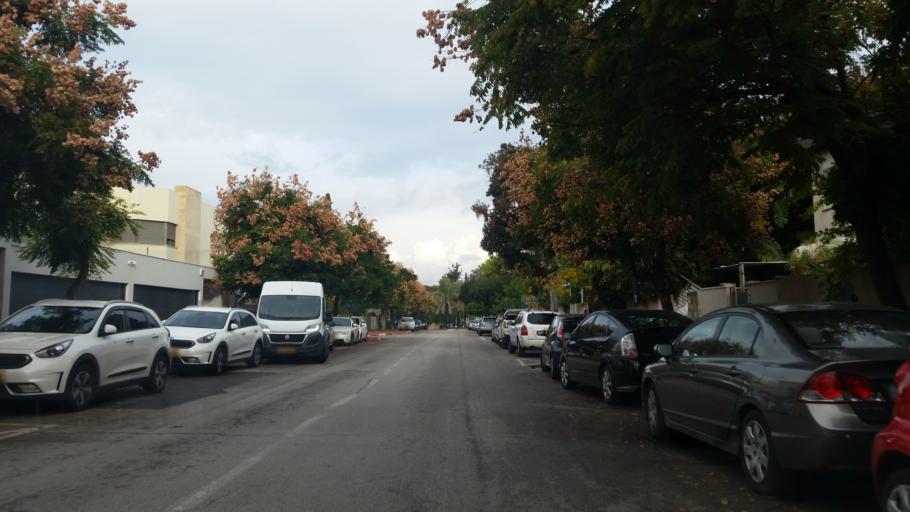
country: IL
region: Tel Aviv
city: Ramat HaSharon
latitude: 32.1523
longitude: 34.8480
